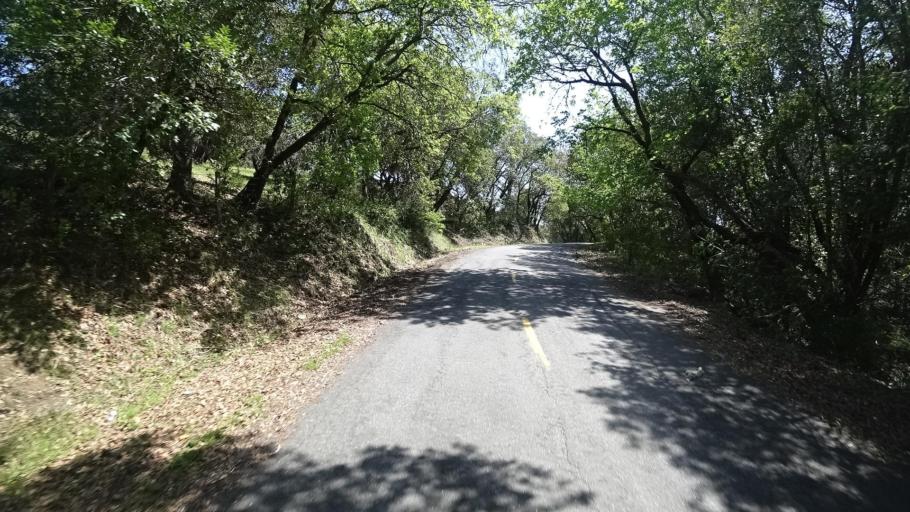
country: US
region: California
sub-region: Humboldt County
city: Redway
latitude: 40.2598
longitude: -123.6263
